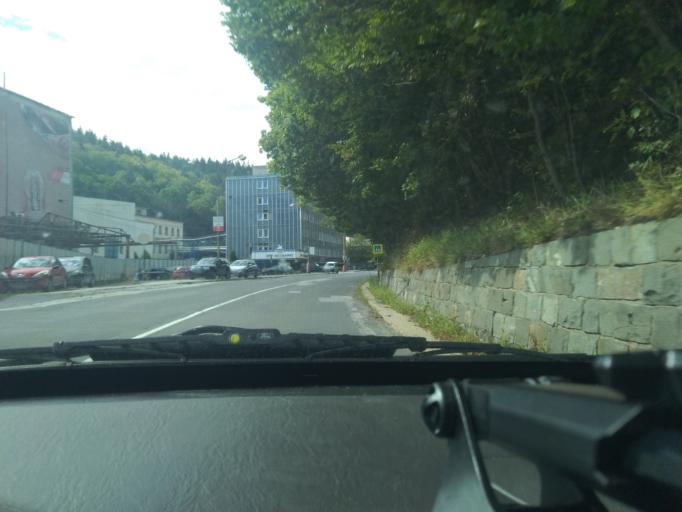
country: SK
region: Banskobystricky
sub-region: Okres Banska Bystrica
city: Banska Bystrica
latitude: 48.7944
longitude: 19.0827
